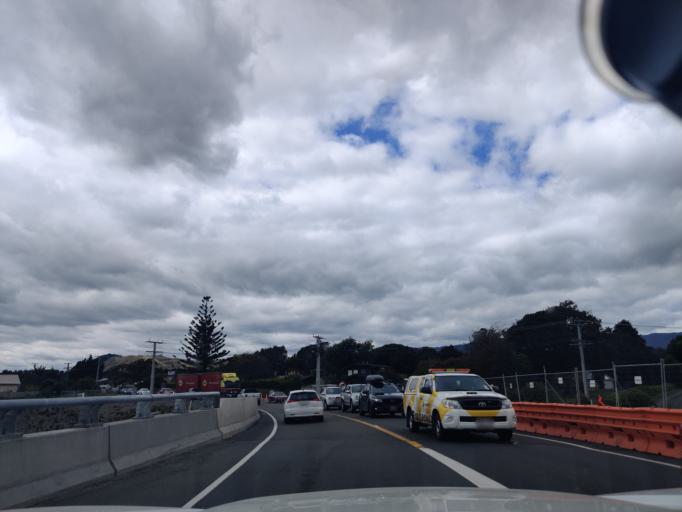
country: NZ
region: Wellington
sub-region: Kapiti Coast District
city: Otaki
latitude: -40.7582
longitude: 175.1611
